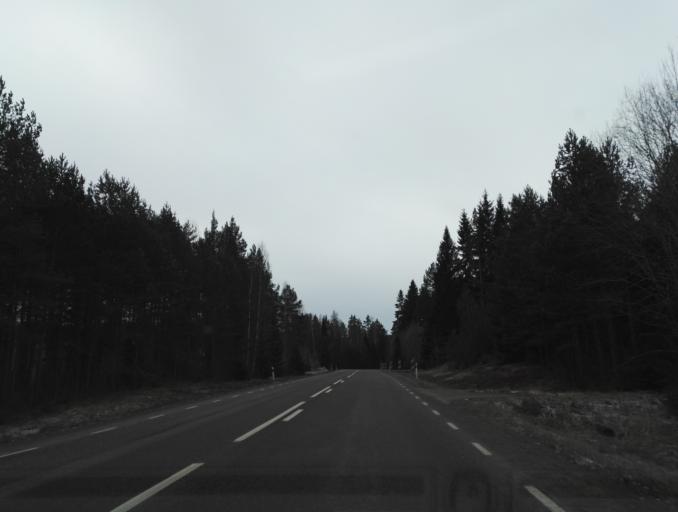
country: SE
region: Kalmar
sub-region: Hultsfreds Kommun
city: Virserum
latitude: 57.3386
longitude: 15.6032
